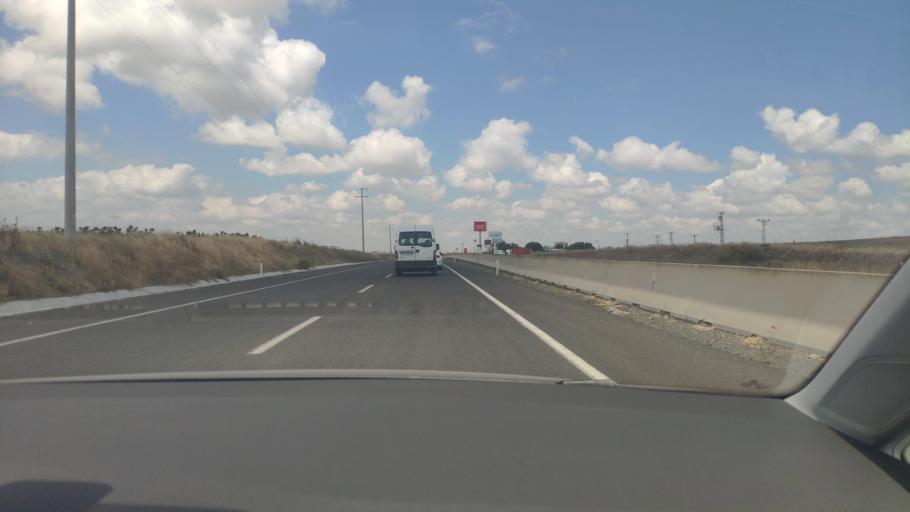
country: TR
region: Tekirdag
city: Sultankoy
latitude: 41.1032
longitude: 27.9423
